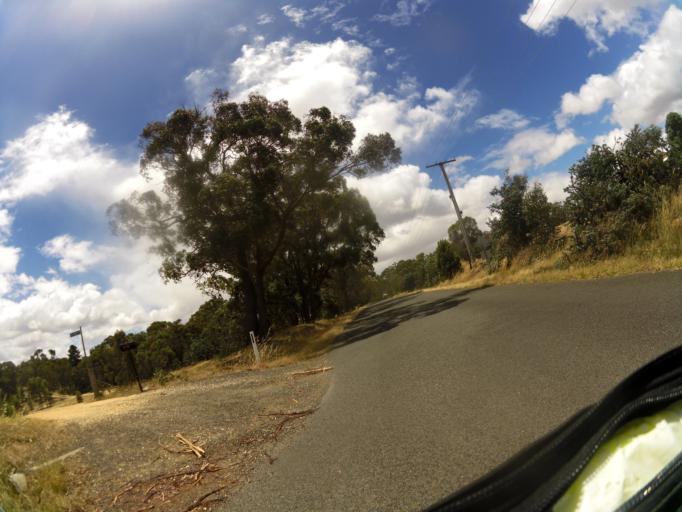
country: AU
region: Victoria
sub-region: Mount Alexander
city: Castlemaine
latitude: -37.0211
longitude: 144.2493
